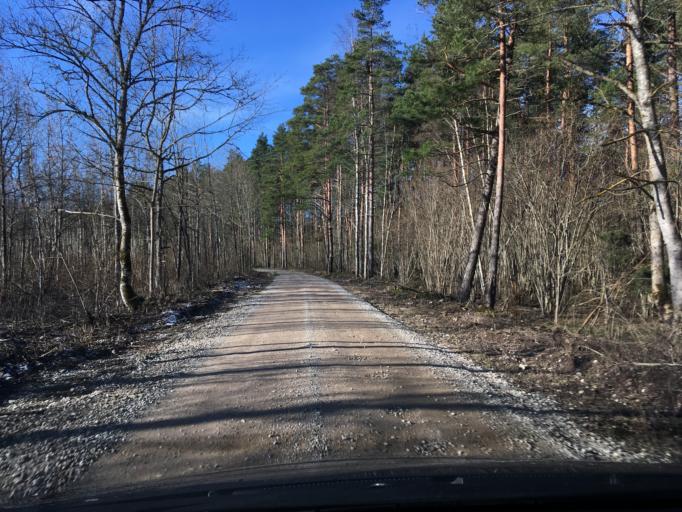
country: EE
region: Laeaene
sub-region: Lihula vald
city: Lihula
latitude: 58.5726
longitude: 23.6959
